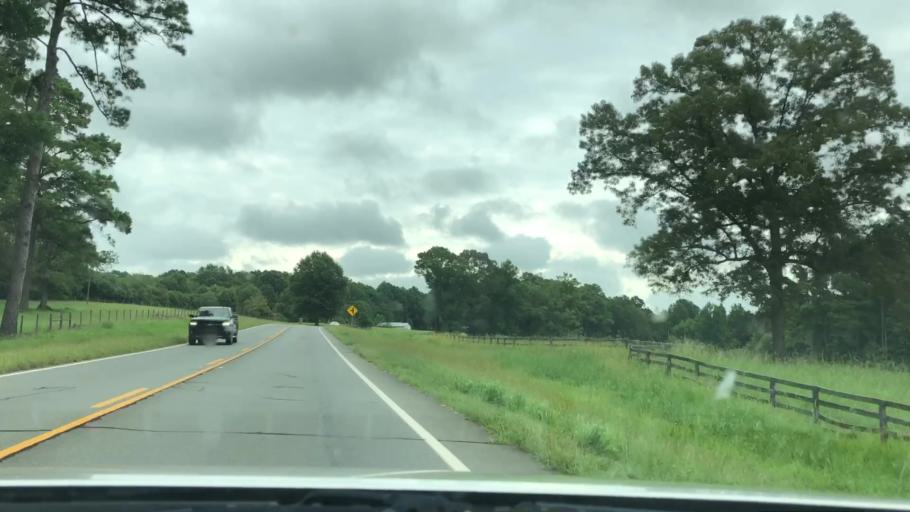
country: US
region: Georgia
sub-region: Pike County
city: Zebulon
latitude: 33.1083
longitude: -84.3694
